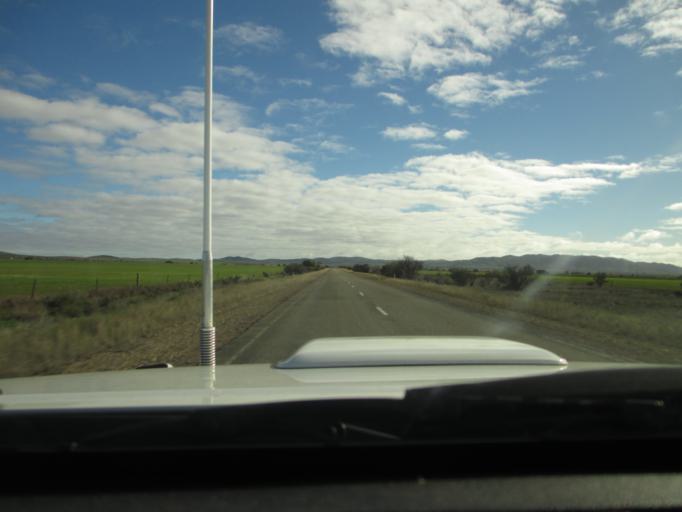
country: AU
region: South Australia
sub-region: Peterborough
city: Peterborough
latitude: -32.6560
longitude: 138.6035
